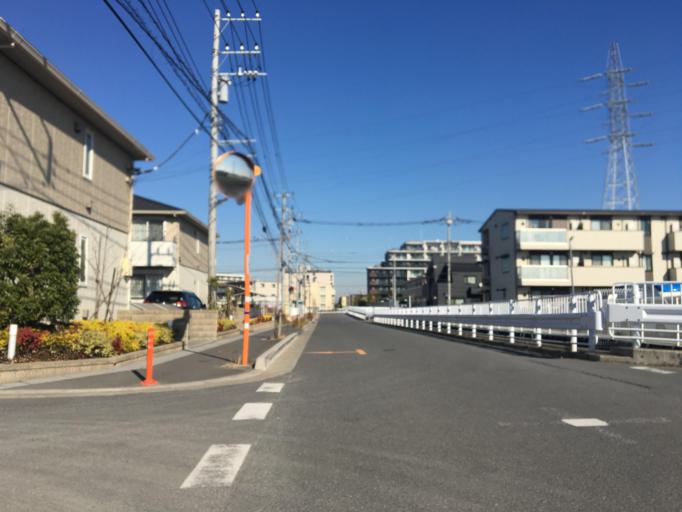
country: JP
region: Saitama
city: Yashio-shi
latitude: 35.8059
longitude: 139.8489
